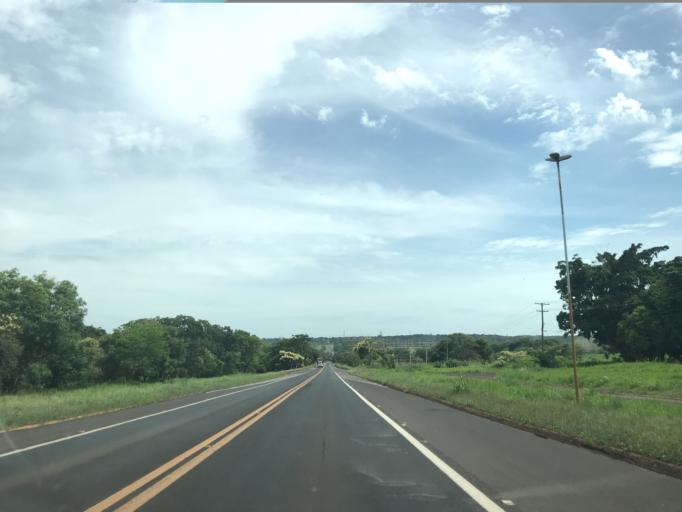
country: BR
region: Sao Paulo
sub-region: Nova Granada
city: Nova Granada
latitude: -20.3184
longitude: -49.2103
